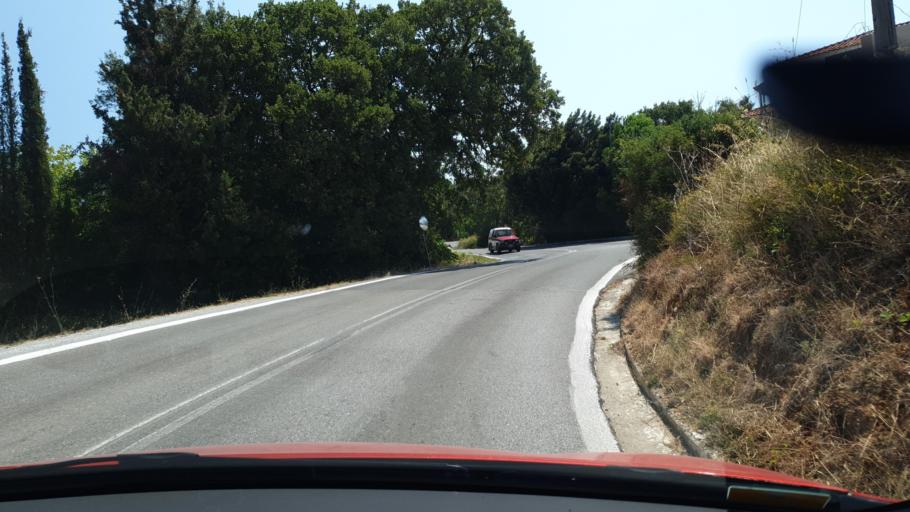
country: GR
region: Central Greece
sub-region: Nomos Evvoias
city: Oxilithos
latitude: 38.5276
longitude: 24.0918
